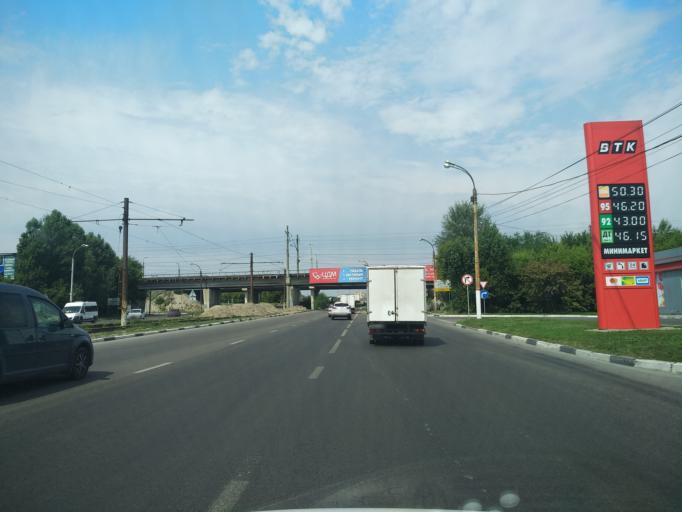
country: RU
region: Voronezj
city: Voronezh
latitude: 51.6945
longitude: 39.2302
